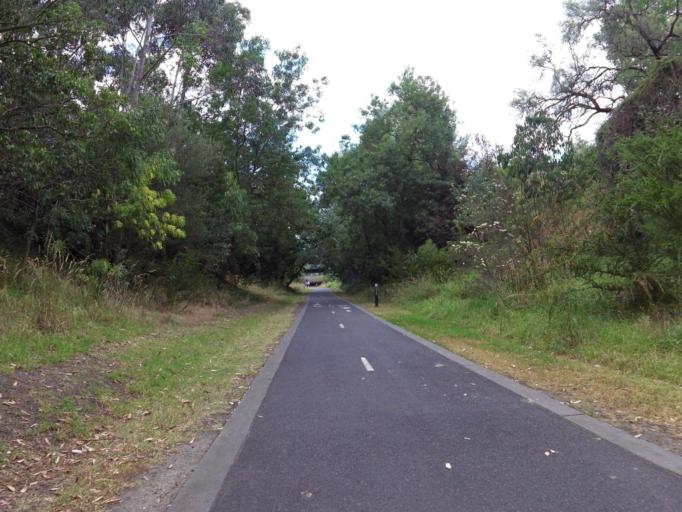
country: AU
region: Victoria
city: Balwyn
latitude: -37.8180
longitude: 145.0660
